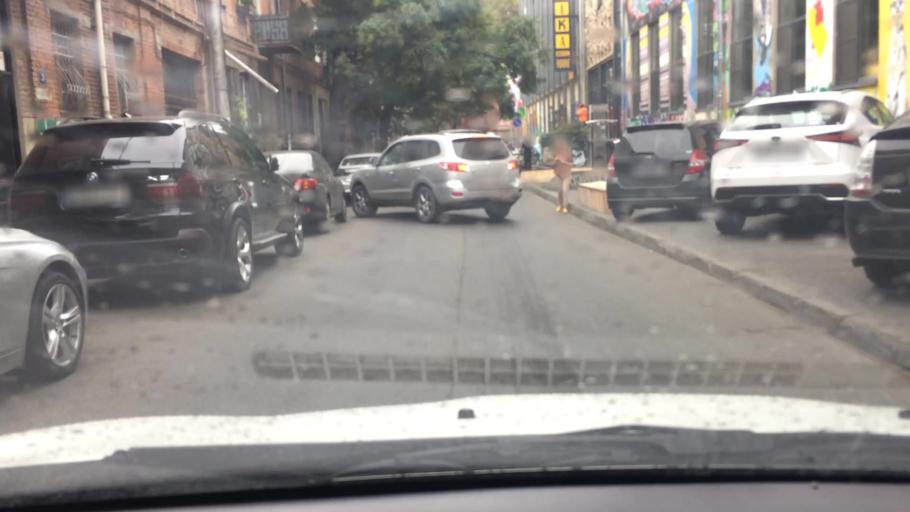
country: GE
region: T'bilisi
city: Tbilisi
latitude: 41.7099
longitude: 44.8027
